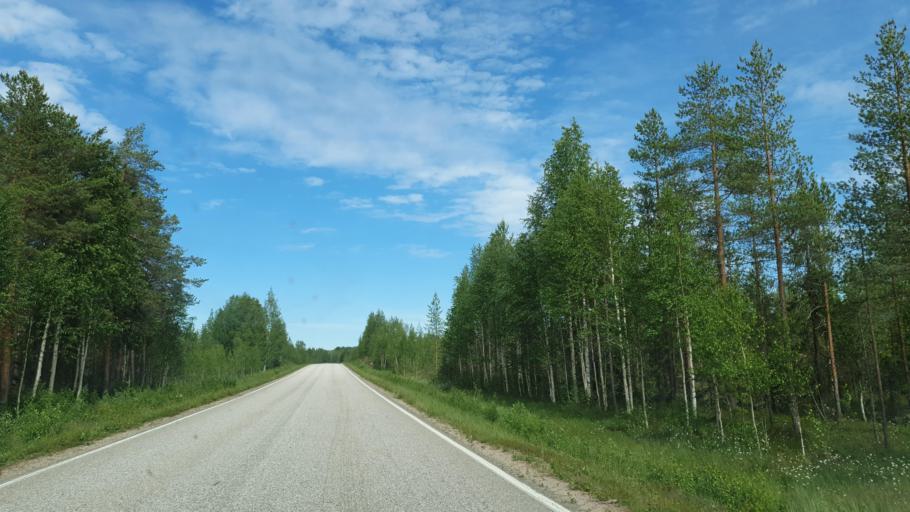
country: FI
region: Kainuu
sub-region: Kehys-Kainuu
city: Suomussalmi
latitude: 64.5666
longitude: 28.9795
